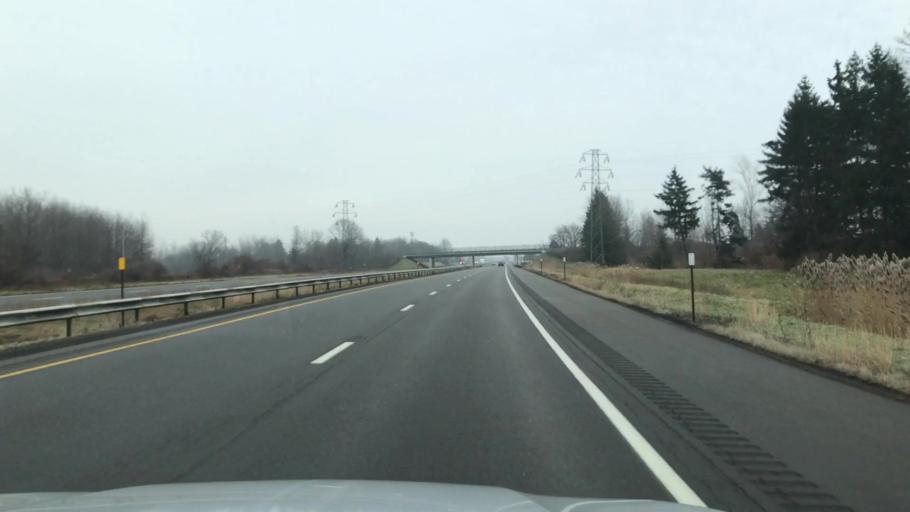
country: US
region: New York
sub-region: Chautauqua County
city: Silver Creek
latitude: 42.5124
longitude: -79.1933
